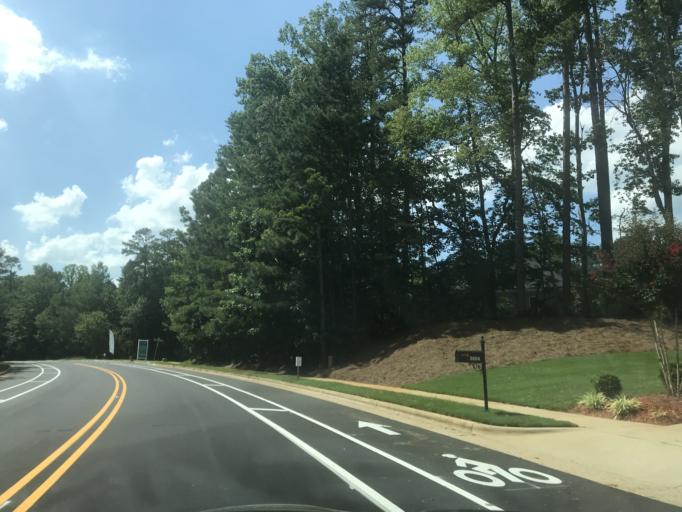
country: US
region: North Carolina
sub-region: Wake County
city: West Raleigh
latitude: 35.8860
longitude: -78.7132
